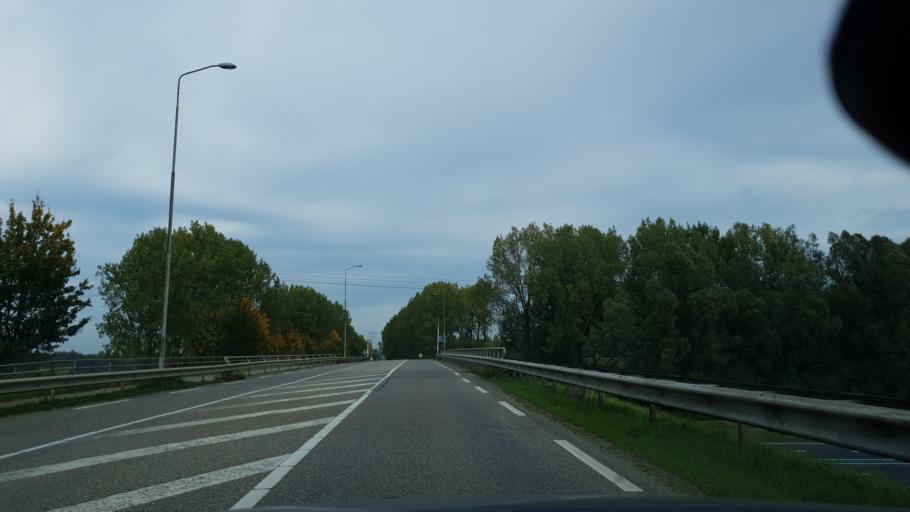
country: NL
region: Gelderland
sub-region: Gemeente Wijchen
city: Bergharen
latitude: 51.8718
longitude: 5.6600
